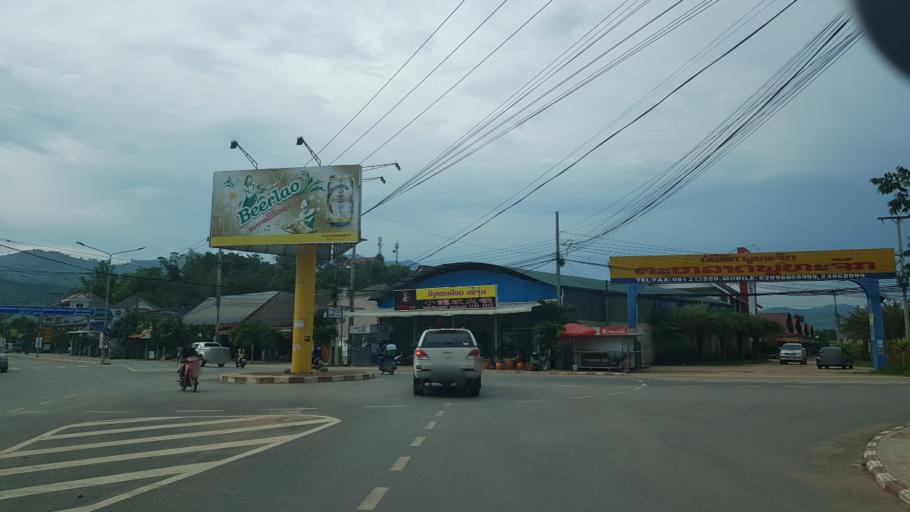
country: LA
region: Oudomxai
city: Muang Xay
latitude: 20.6852
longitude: 101.9877
